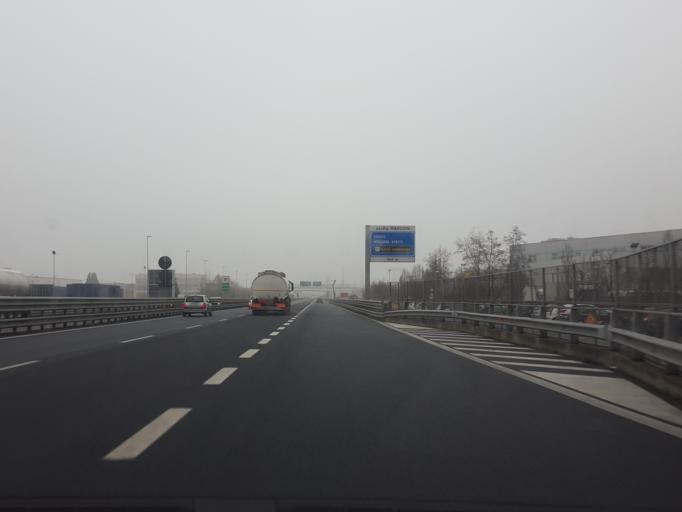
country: IT
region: Veneto
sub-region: Provincia di Venezia
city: Dese
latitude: 45.5423
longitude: 12.2923
